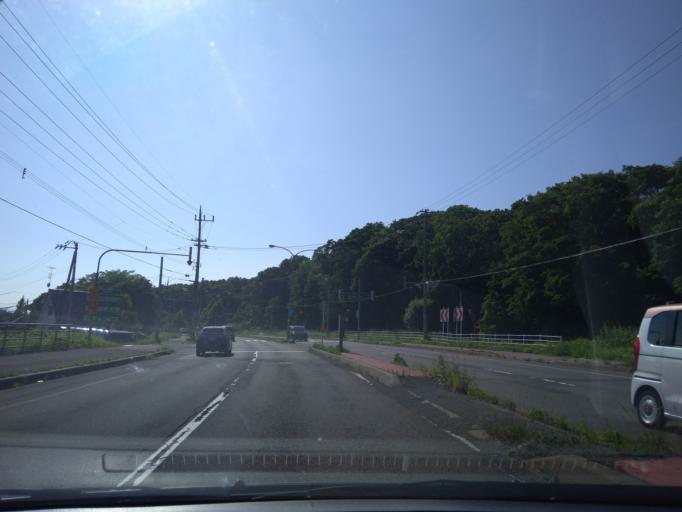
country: JP
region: Hokkaido
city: Kitahiroshima
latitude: 42.9821
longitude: 141.5344
